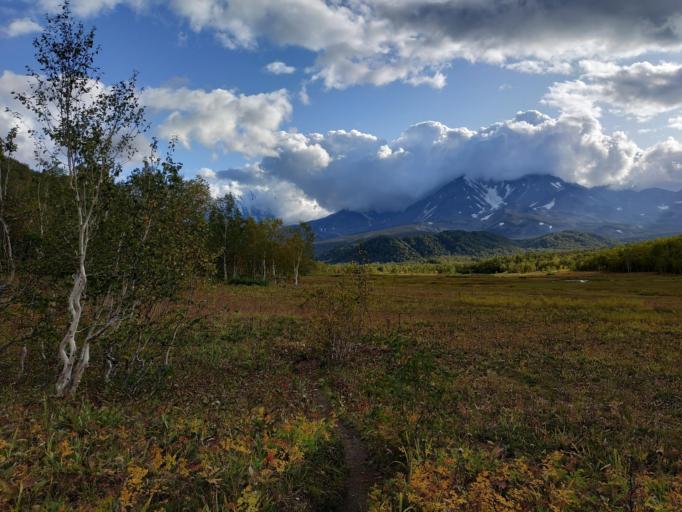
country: RU
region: Kamtsjatka
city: Petropavlovsk-Kamchatsky
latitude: 53.4706
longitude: 158.7295
